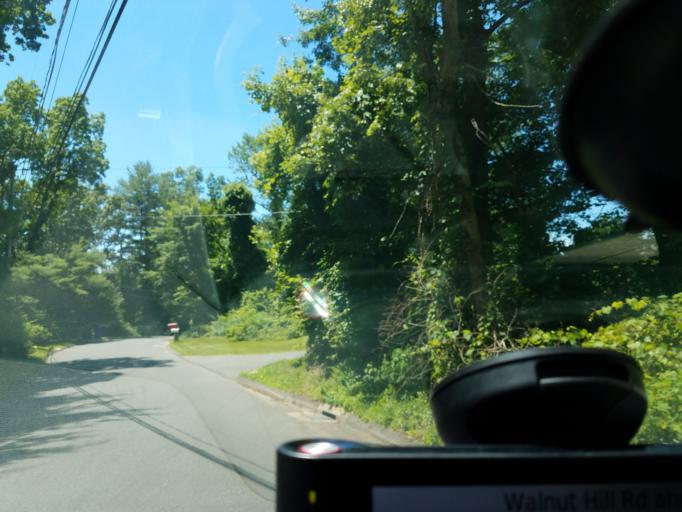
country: US
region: Connecticut
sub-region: Fairfield County
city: Bethel
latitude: 41.3930
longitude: -73.3928
